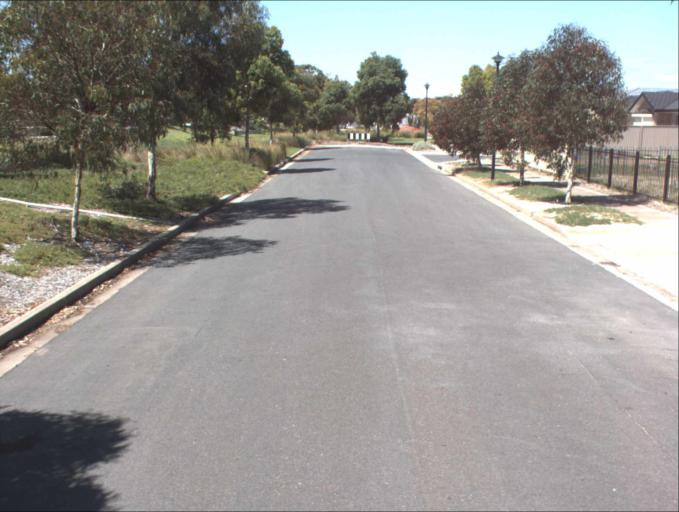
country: AU
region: South Australia
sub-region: Charles Sturt
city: Woodville North
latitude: -34.8563
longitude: 138.5524
